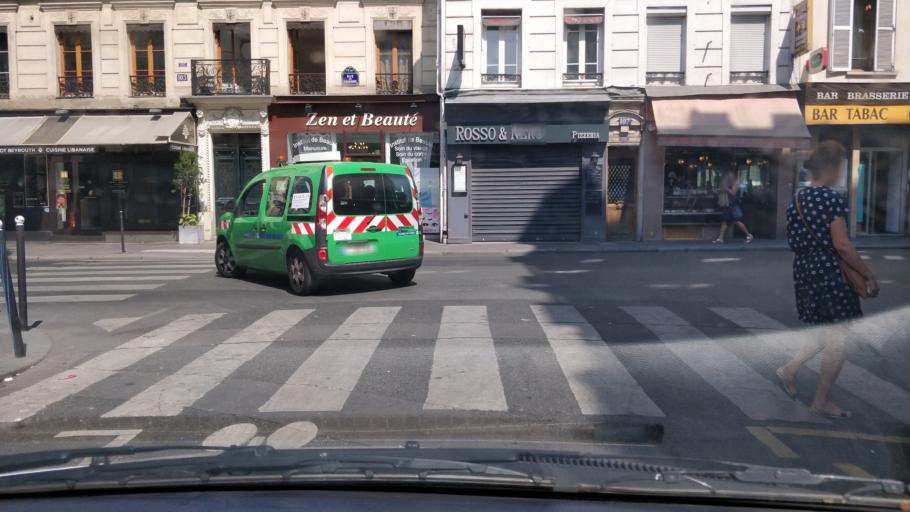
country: FR
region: Ile-de-France
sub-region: Departement de Seine-Saint-Denis
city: Bagnolet
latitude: 48.8542
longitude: 2.3848
